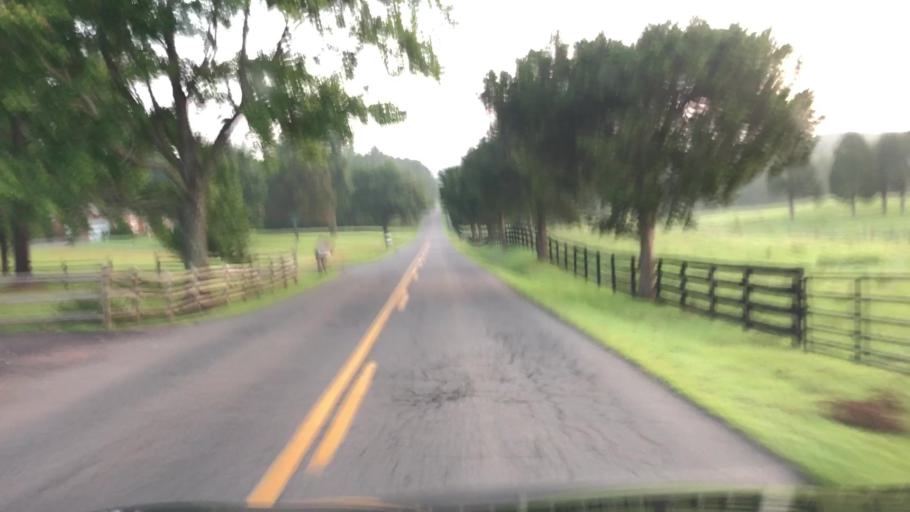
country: US
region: Virginia
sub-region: Prince William County
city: Nokesville
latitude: 38.7078
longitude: -77.6653
